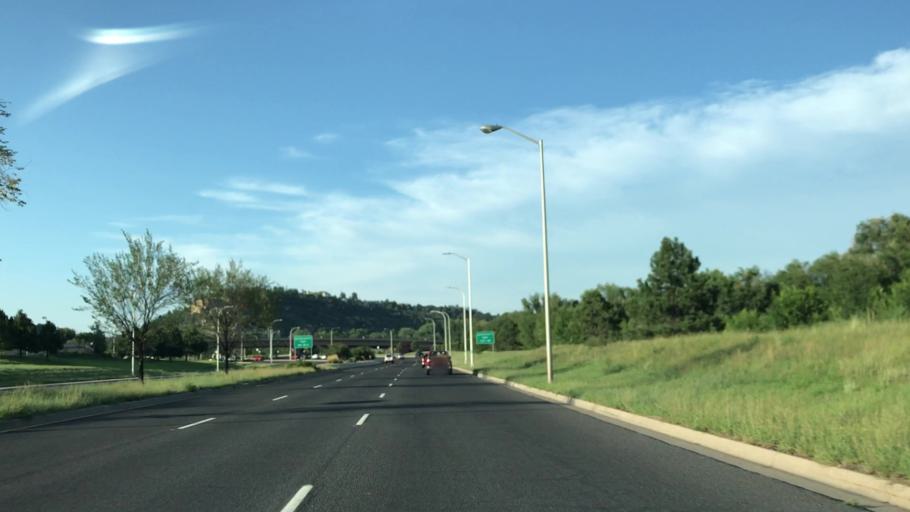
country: US
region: Colorado
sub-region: El Paso County
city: Colorado Springs
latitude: 38.8858
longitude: -104.7876
